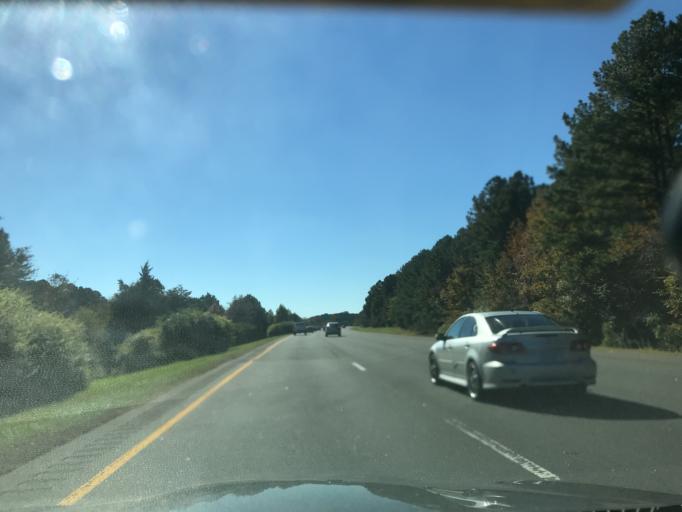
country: US
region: North Carolina
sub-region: Durham County
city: Durham
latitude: 35.9092
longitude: -78.8672
